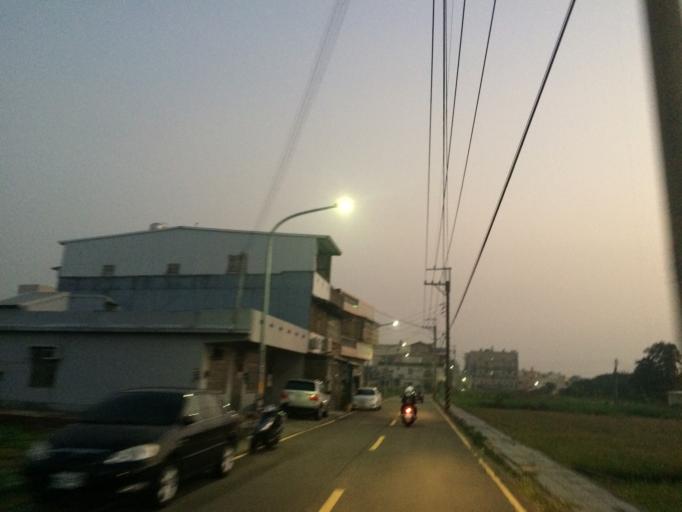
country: TW
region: Taiwan
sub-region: Hsinchu
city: Hsinchu
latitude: 24.7722
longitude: 120.9154
